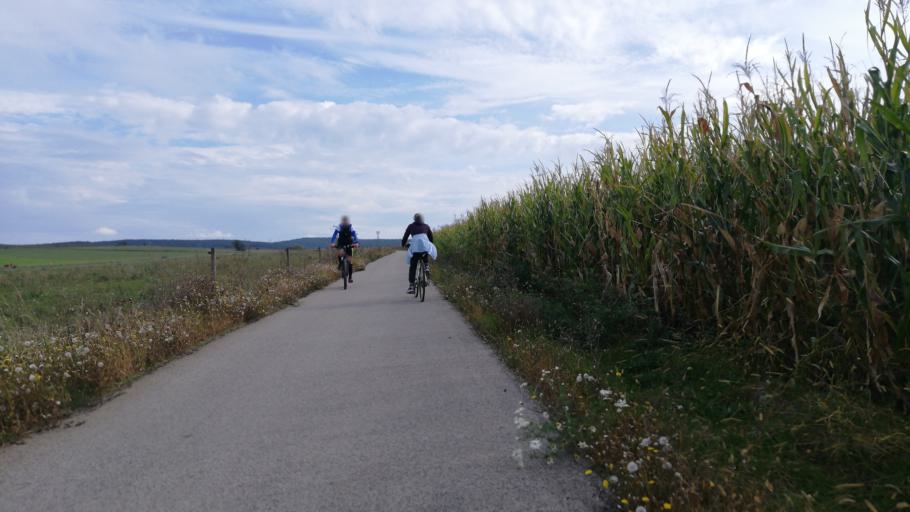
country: CZ
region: South Moravian
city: Sudomerice
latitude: 48.8439
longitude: 17.2766
